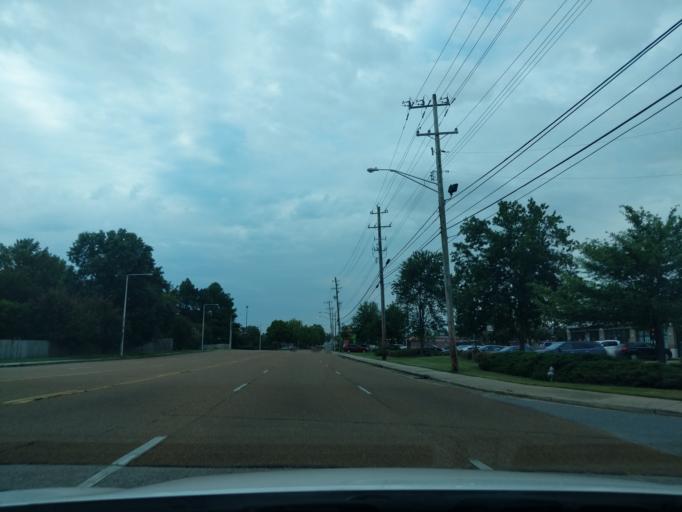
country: US
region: Tennessee
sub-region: Shelby County
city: Germantown
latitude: 35.0729
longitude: -89.8425
